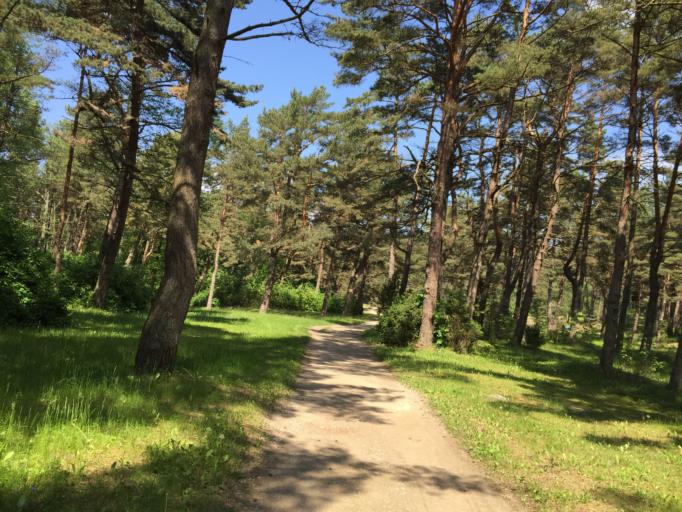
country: LT
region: Klaipedos apskritis
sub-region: Klaipeda
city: Palanga
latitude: 55.9034
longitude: 21.0525
